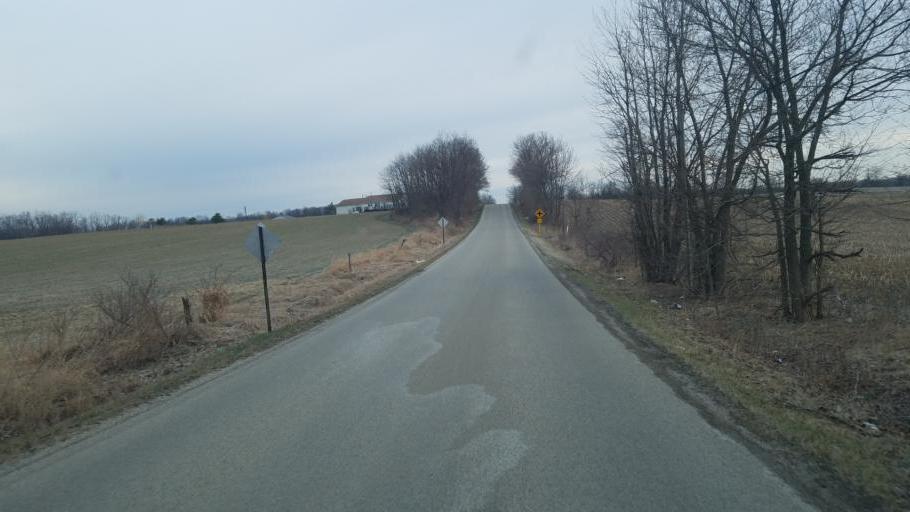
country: US
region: Ohio
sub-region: Morrow County
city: Cardington
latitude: 40.4300
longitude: -82.8089
